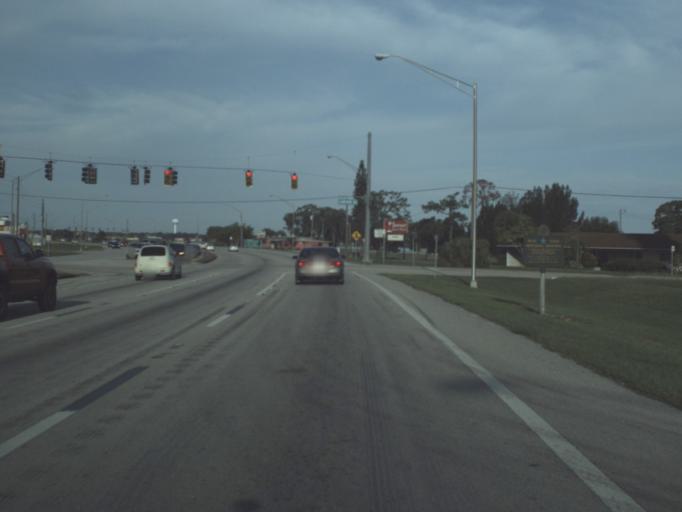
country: US
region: Florida
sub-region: Highlands County
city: Sebring
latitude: 27.4725
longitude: -81.4458
